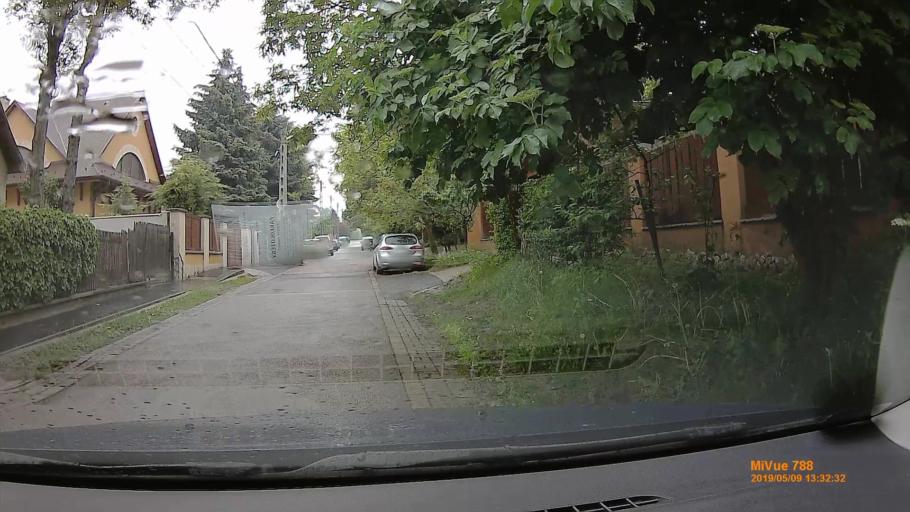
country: HU
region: Pest
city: Csomor
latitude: 47.5336
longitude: 19.2020
